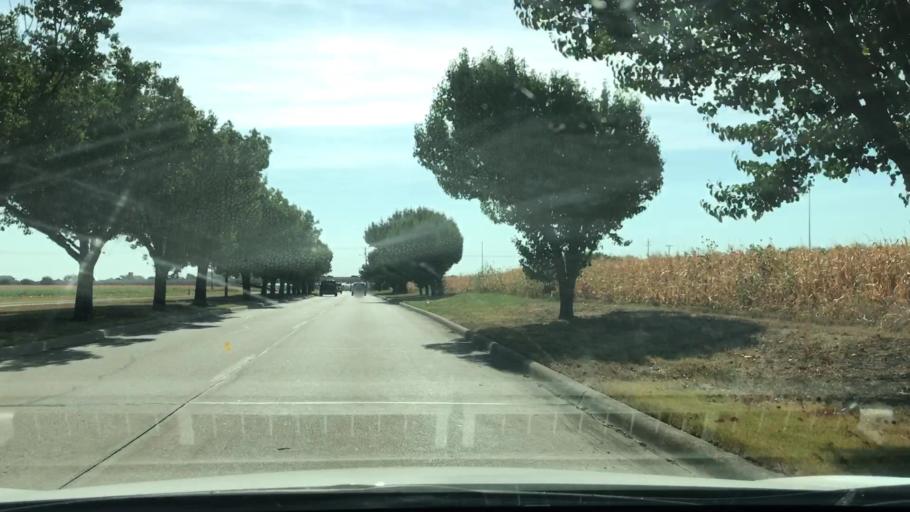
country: US
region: Texas
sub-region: Collin County
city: McKinney
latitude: 33.2291
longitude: -96.6378
